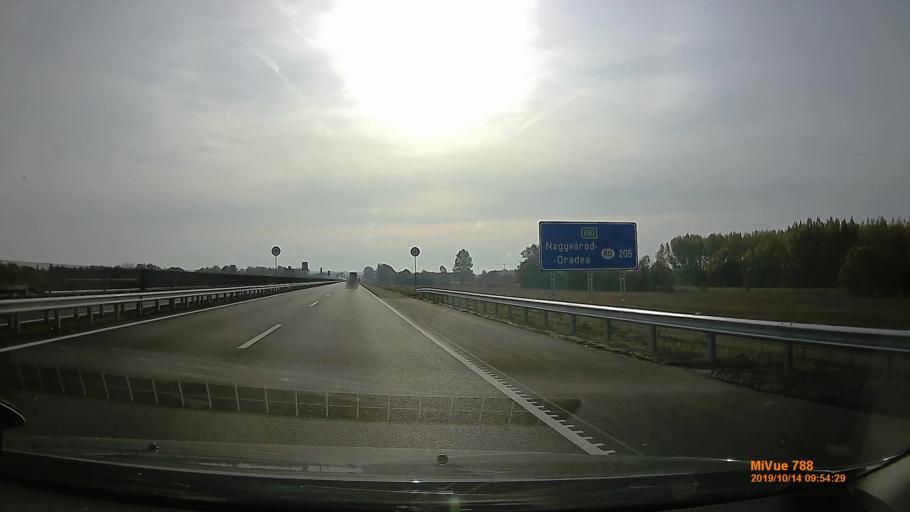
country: HU
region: Pest
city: Albertirsa
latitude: 47.2601
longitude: 19.6252
